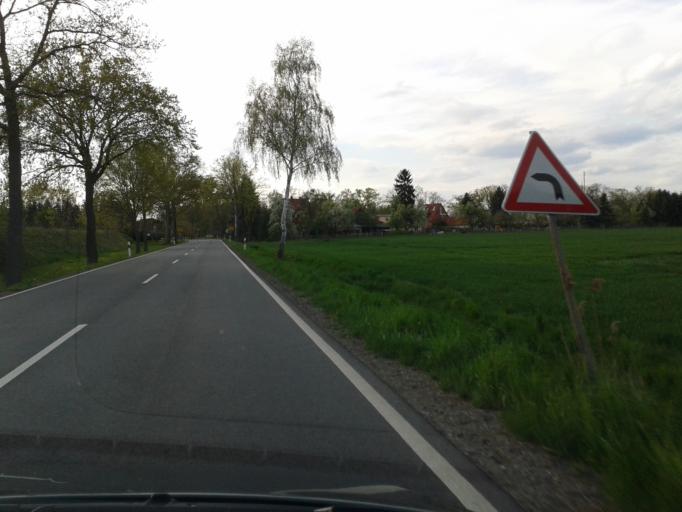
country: DE
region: Lower Saxony
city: Wustrow
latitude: 52.9225
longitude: 11.1353
